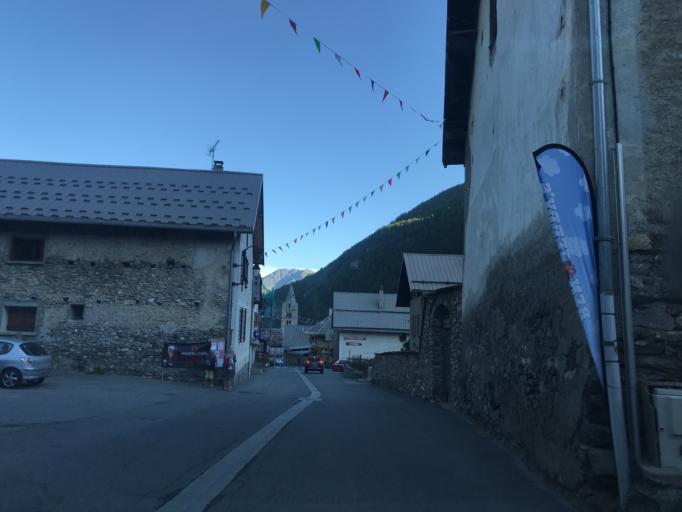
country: FR
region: Provence-Alpes-Cote d'Azur
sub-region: Departement des Hautes-Alpes
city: Guillestre
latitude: 44.7678
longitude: 6.7382
